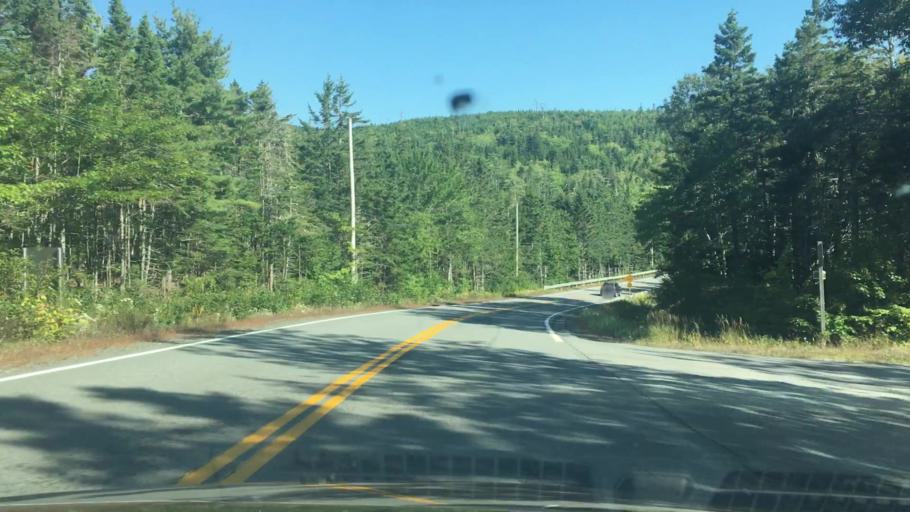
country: CA
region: Nova Scotia
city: Cole Harbour
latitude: 44.8145
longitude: -62.8856
